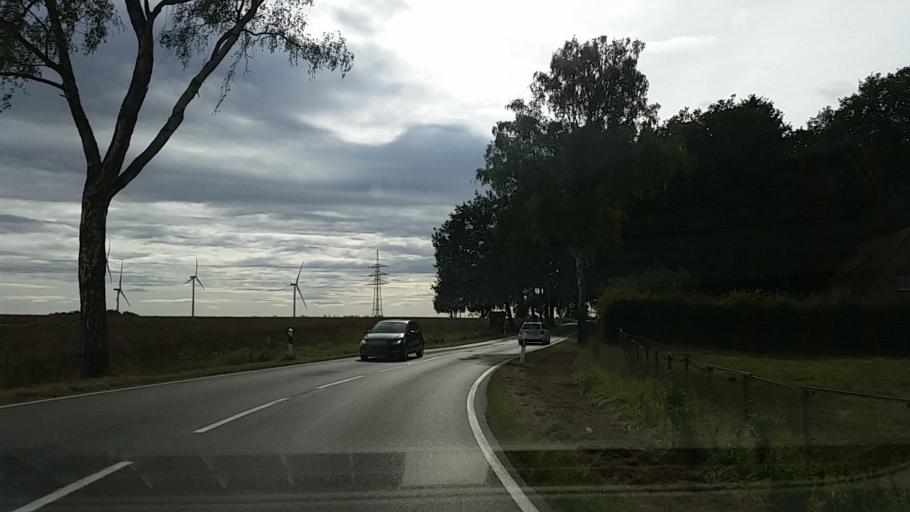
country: DE
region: Lower Saxony
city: Ebstorf
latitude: 52.9982
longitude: 10.4121
